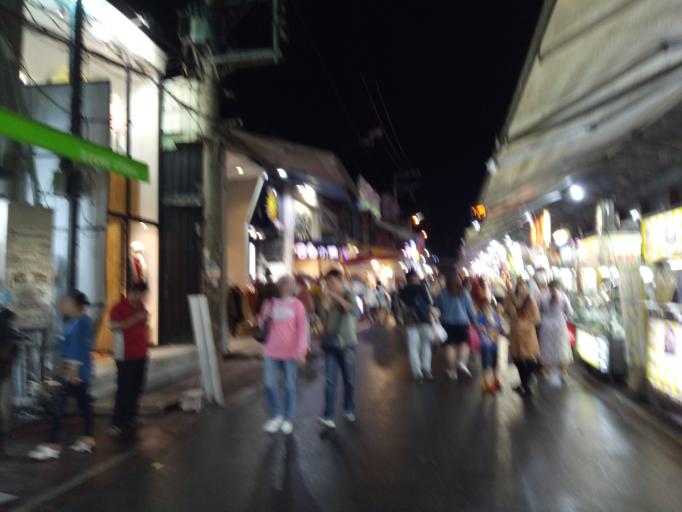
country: TW
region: Taiwan
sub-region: Taichung City
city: Taichung
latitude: 24.1771
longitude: 120.6469
